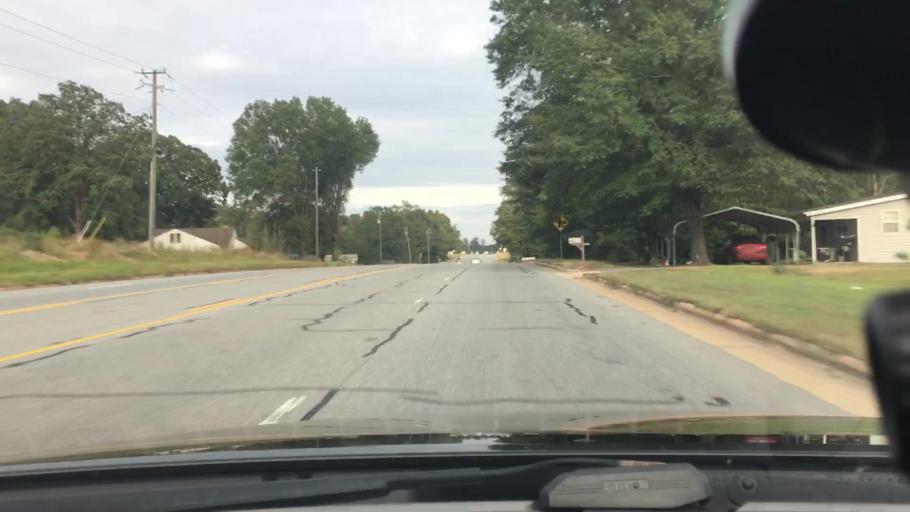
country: US
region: North Carolina
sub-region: Montgomery County
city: Biscoe
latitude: 35.3557
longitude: -79.8102
